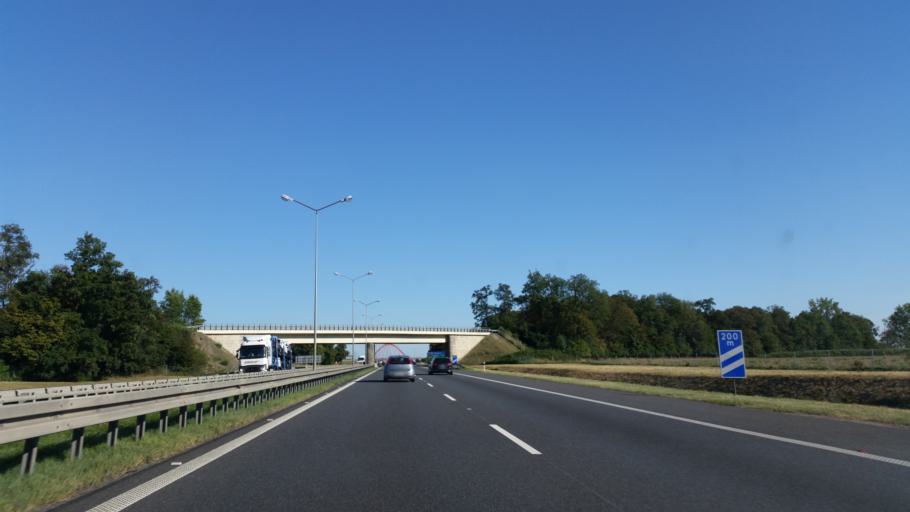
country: PL
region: Lower Silesian Voivodeship
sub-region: Powiat olawski
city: Wierzbno
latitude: 50.8835
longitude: 17.1963
